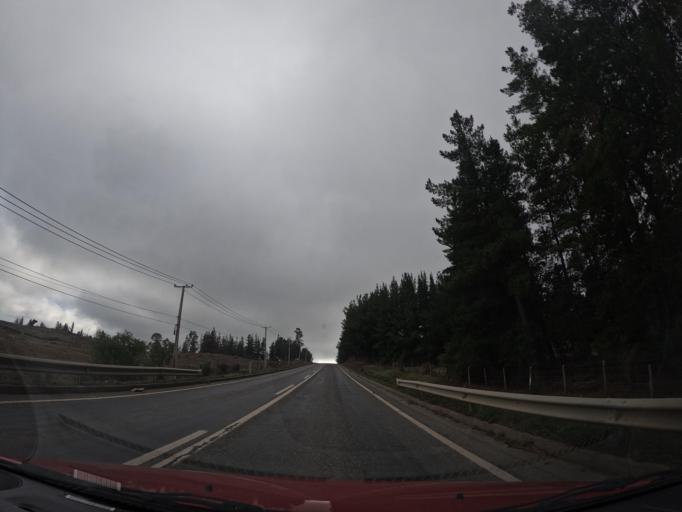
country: CL
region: Maule
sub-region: Provincia de Cauquenes
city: Cauquenes
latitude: -36.2503
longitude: -72.5483
